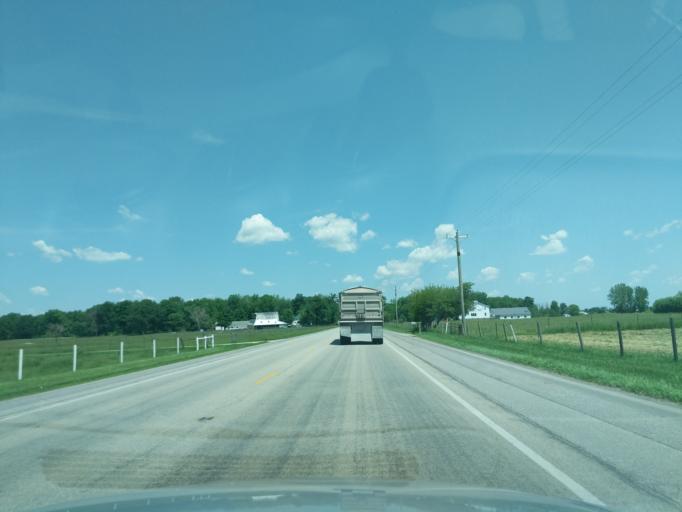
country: US
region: Indiana
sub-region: LaGrange County
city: Topeka
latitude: 41.5602
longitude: -85.5784
